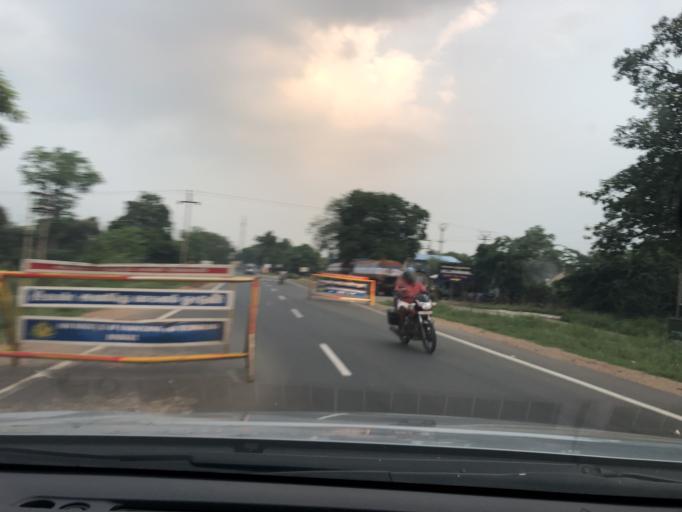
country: IN
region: Tamil Nadu
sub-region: Dindigul
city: Vedasandur
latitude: 10.4325
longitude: 77.8624
